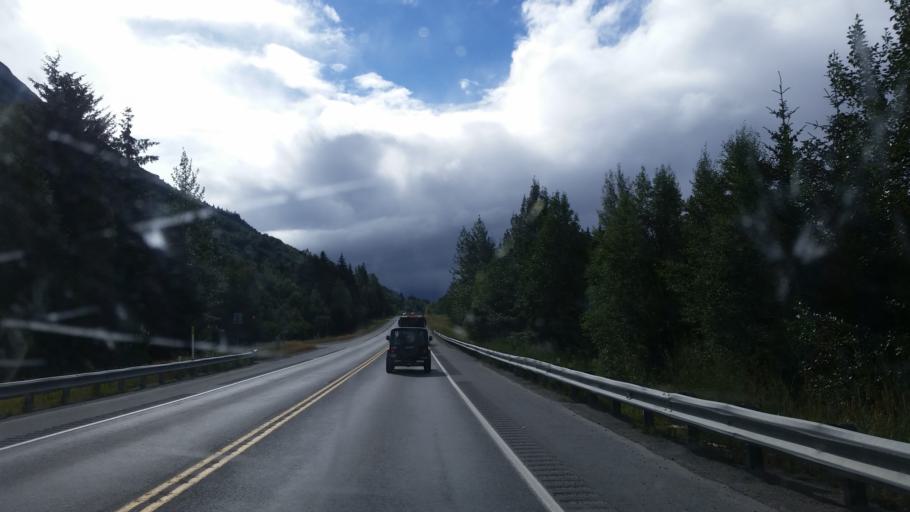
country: US
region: Alaska
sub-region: Anchorage Municipality
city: Girdwood
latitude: 60.9668
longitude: -149.4434
